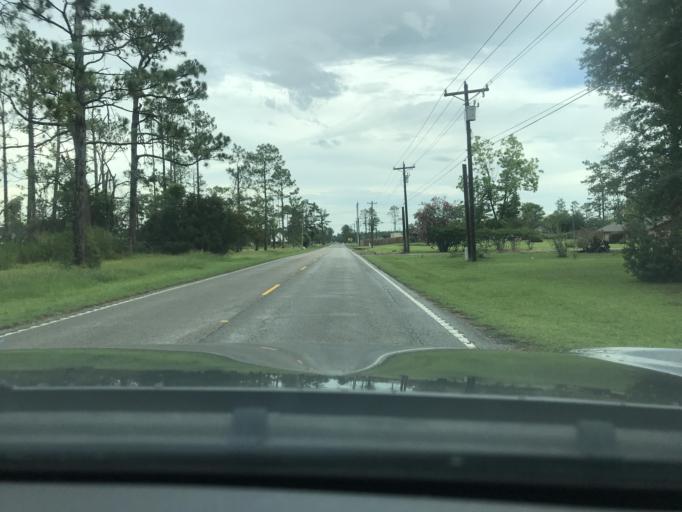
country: US
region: Louisiana
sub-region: Calcasieu Parish
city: Moss Bluff
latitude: 30.3257
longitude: -93.2581
